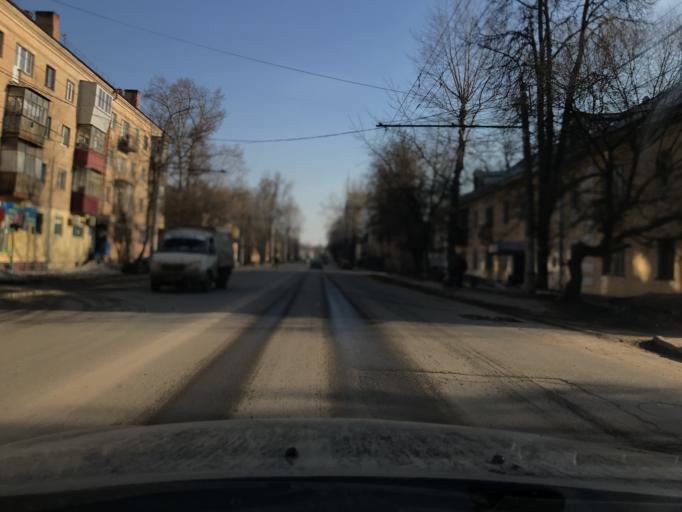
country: RU
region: Kaluga
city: Kaluga
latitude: 54.5311
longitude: 36.2612
